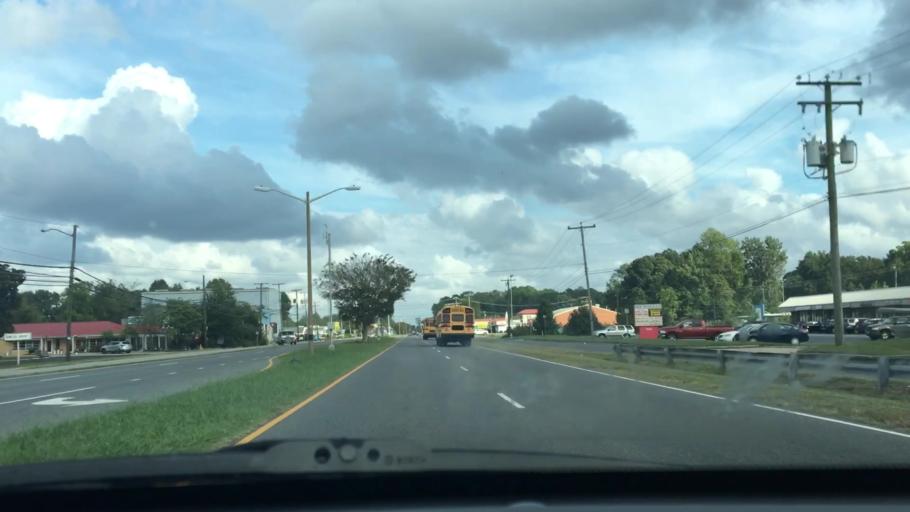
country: US
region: Virginia
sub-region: City of Portsmouth
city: Portsmouth Heights
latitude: 36.7725
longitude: -76.3391
